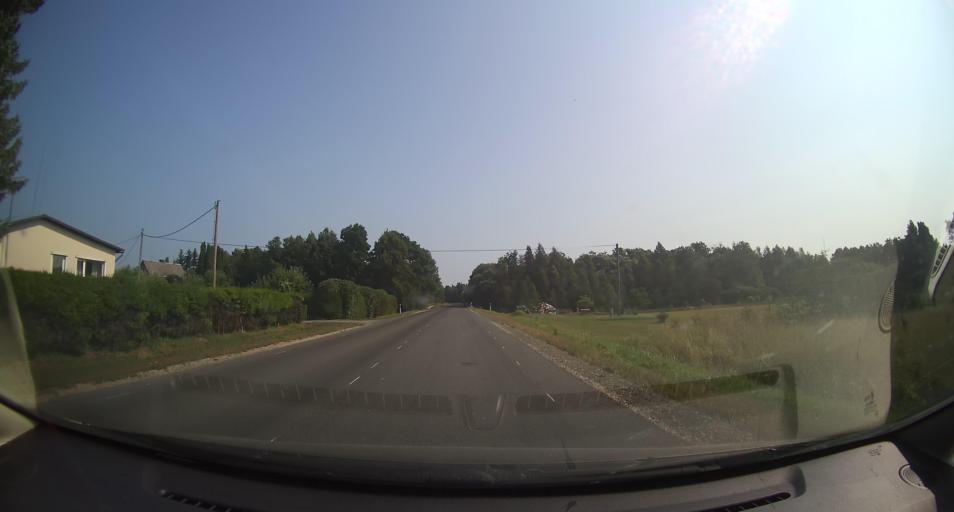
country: EE
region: Paernumaa
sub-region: Audru vald
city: Audru
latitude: 58.4696
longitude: 24.3194
